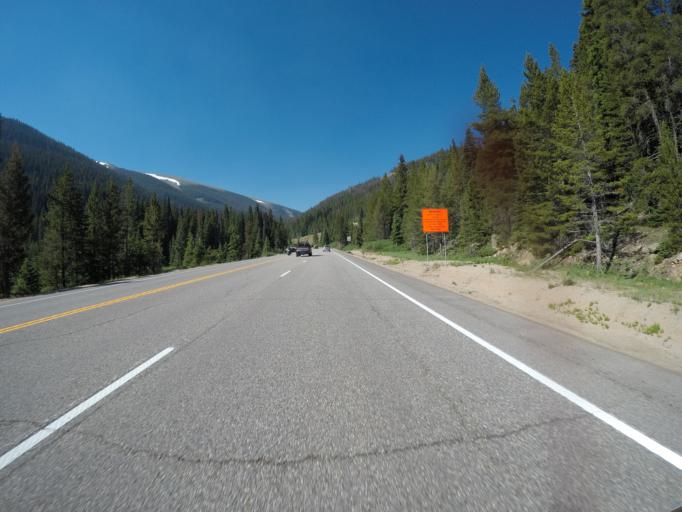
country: US
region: Colorado
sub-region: Grand County
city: Fraser
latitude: 39.8314
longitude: -105.7584
